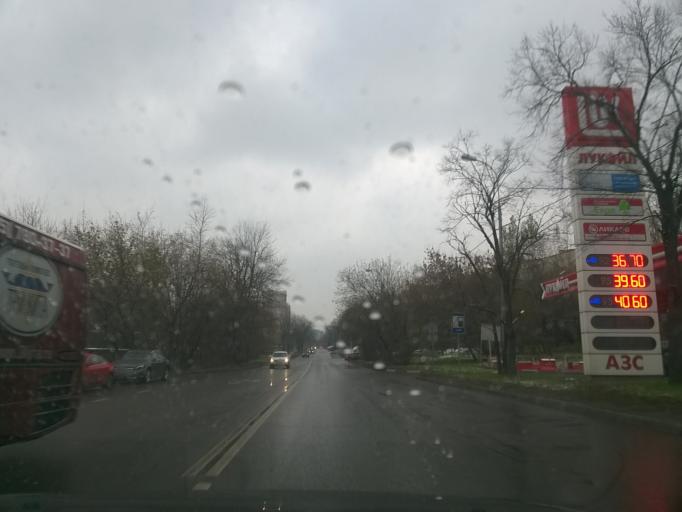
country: RU
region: Moskovskaya
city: Bol'shaya Setun'
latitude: 55.7306
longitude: 37.4440
